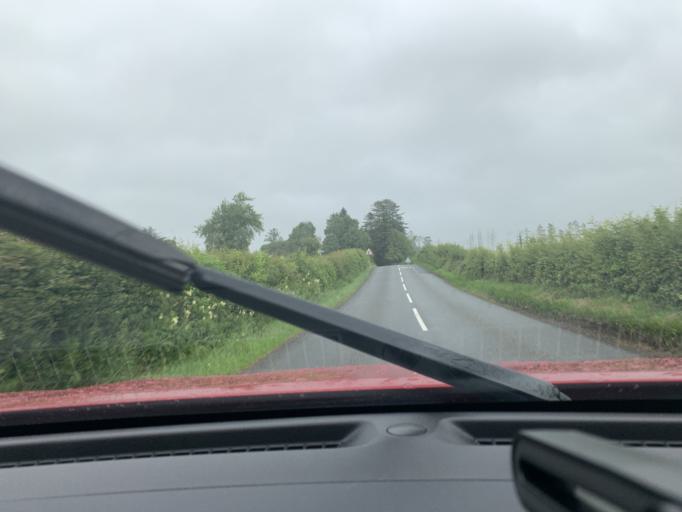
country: GB
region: Northern Ireland
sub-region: Fermanagh District
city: Enniskillen
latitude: 54.3106
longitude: -7.6837
